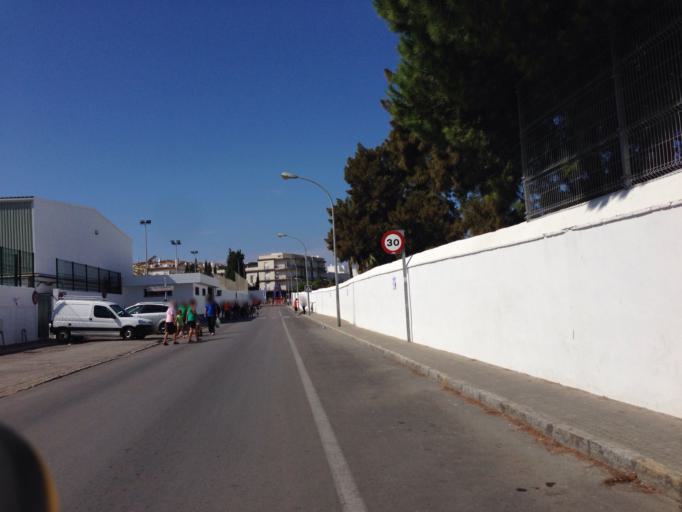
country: ES
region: Andalusia
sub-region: Provincia de Cadiz
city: Chiclana de la Frontera
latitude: 36.4166
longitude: -6.1500
